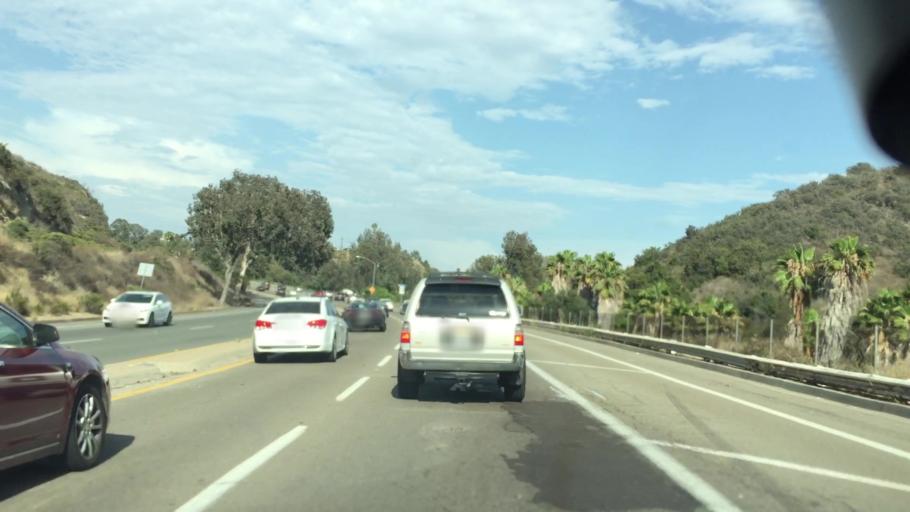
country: US
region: California
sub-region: San Diego County
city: Lemon Grove
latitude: 32.7697
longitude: -117.0904
